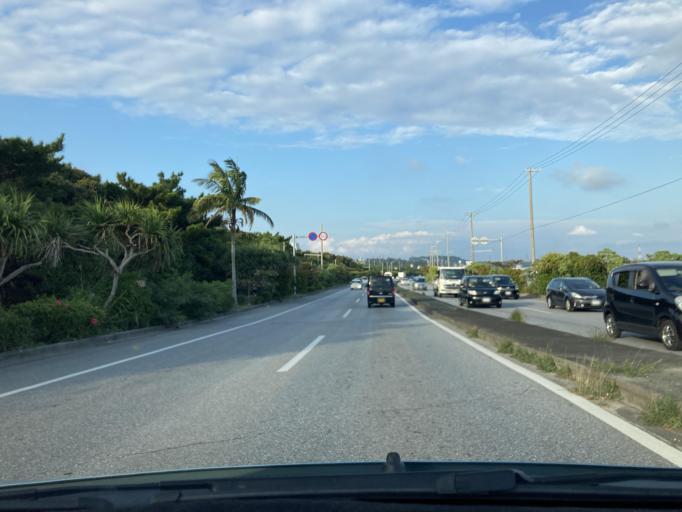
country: JP
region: Okinawa
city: Okinawa
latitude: 26.3263
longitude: 127.8346
